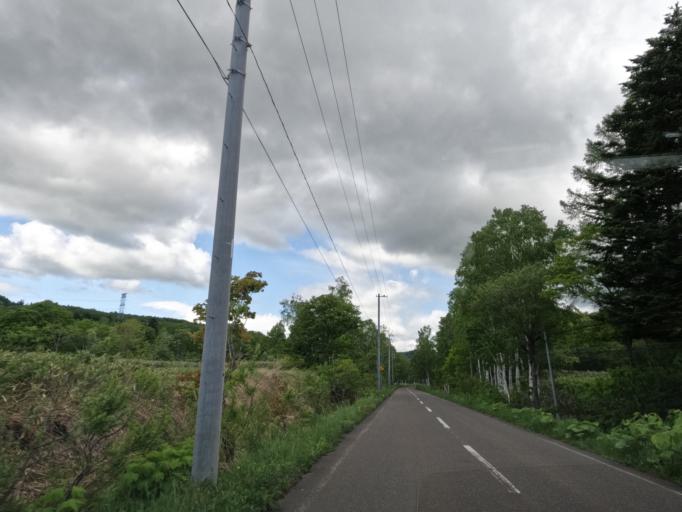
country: JP
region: Hokkaido
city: Tobetsu
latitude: 43.4553
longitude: 141.5914
